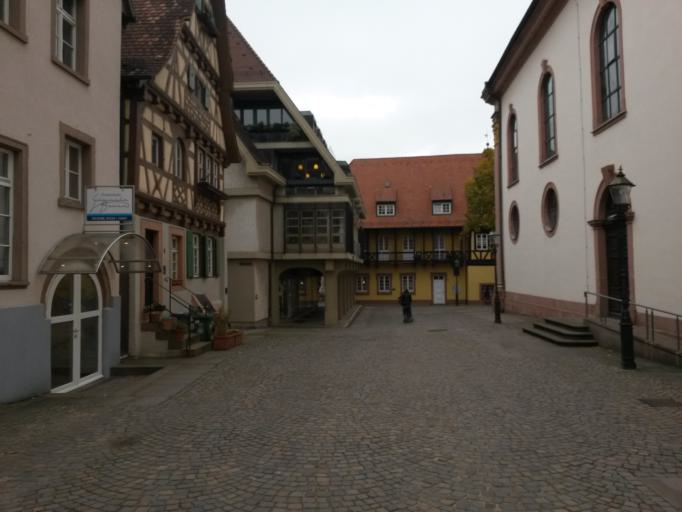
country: DE
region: Baden-Wuerttemberg
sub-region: Karlsruhe Region
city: Ettlingen
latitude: 48.9408
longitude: 8.4087
